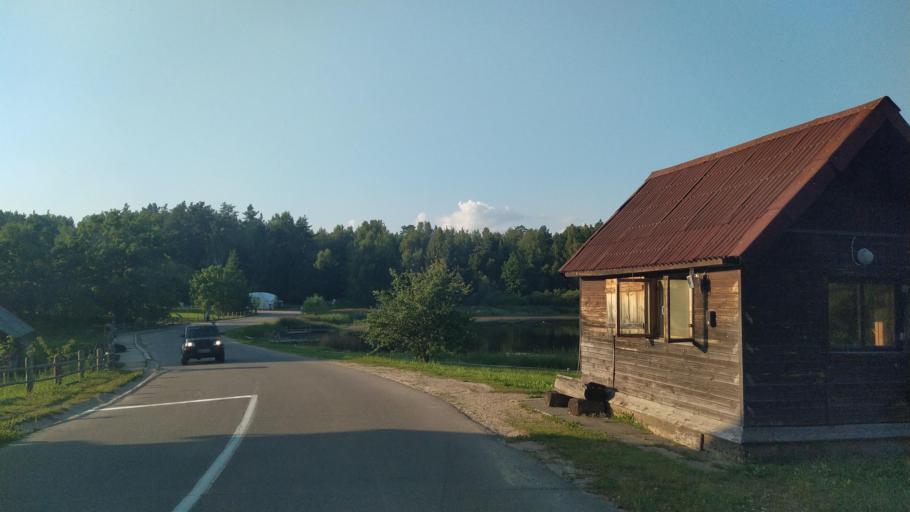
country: RU
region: Pskov
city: Pushkinskiye Gory
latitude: 57.0460
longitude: 28.9180
